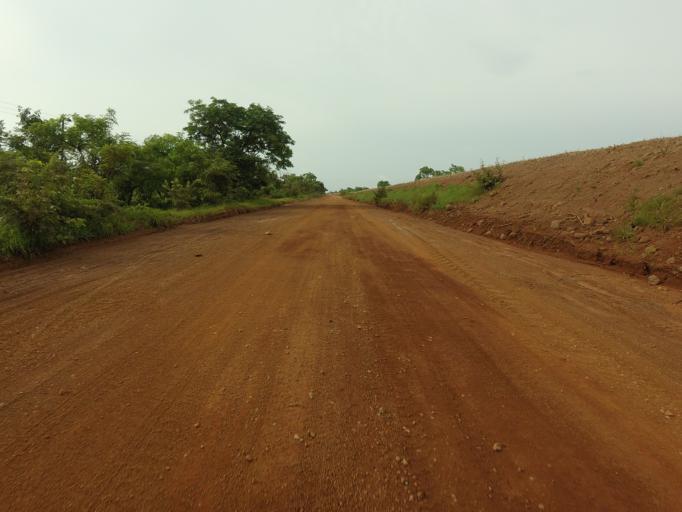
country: GH
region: Northern
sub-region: Yendi
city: Yendi
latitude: 9.6531
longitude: -0.0711
